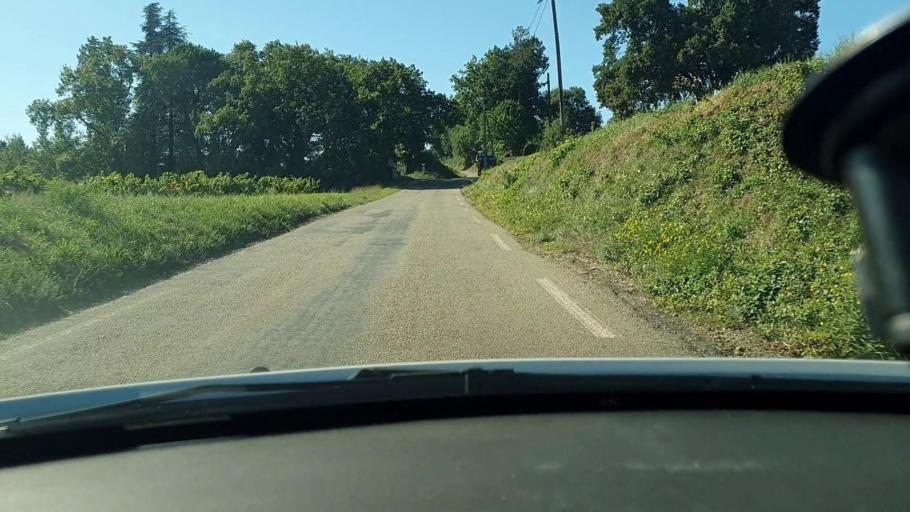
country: FR
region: Languedoc-Roussillon
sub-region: Departement du Gard
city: Saint-Julien-de-Peyrolas
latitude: 44.2773
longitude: 4.5726
